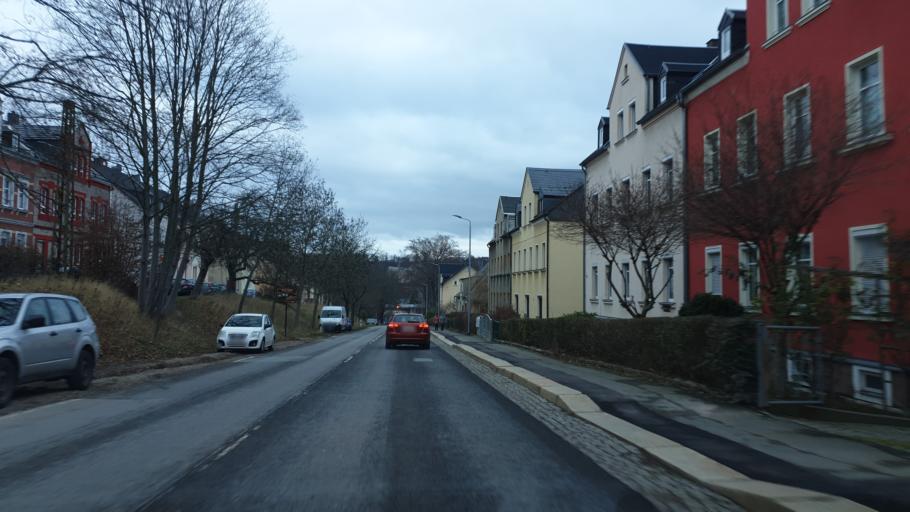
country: DE
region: Saxony
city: Lichtenstein
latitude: 50.7533
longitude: 12.6235
